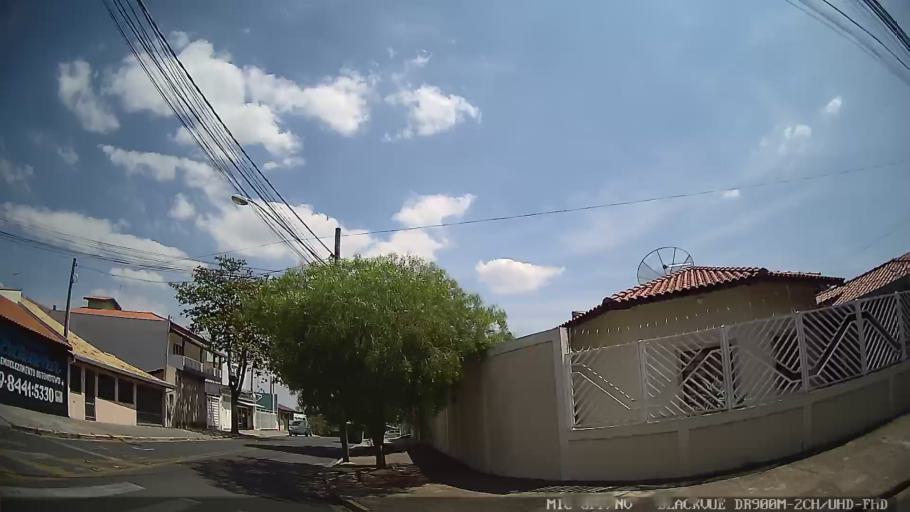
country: BR
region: Sao Paulo
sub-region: Cabreuva
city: Cabreuva
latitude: -23.2570
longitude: -47.0529
